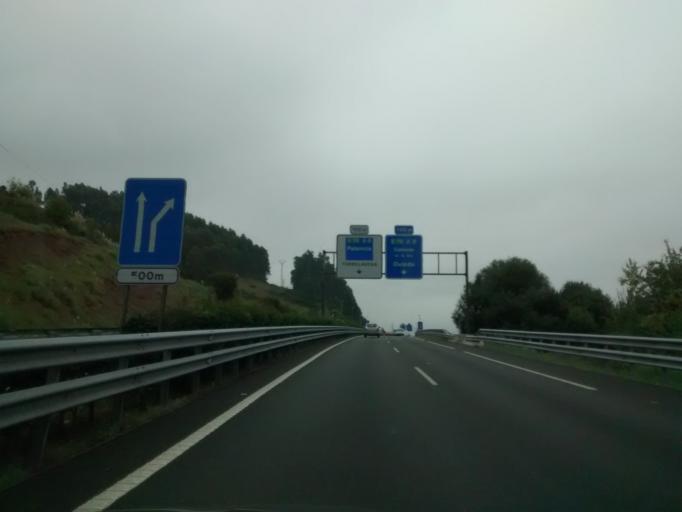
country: ES
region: Cantabria
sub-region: Provincia de Cantabria
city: Torrelavega
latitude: 43.3665
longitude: -4.0416
